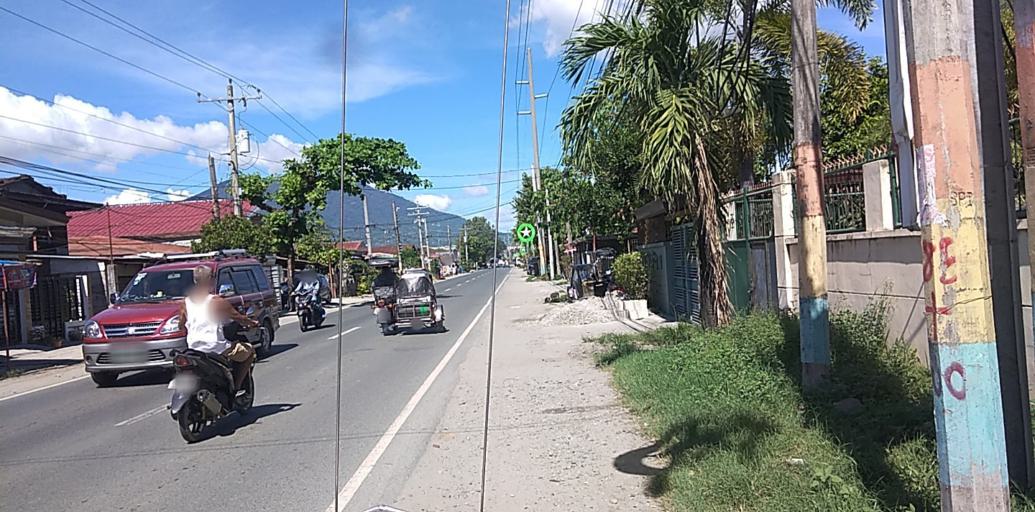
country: PH
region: Central Luzon
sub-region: Province of Pampanga
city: Arayat
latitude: 15.1316
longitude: 120.7748
